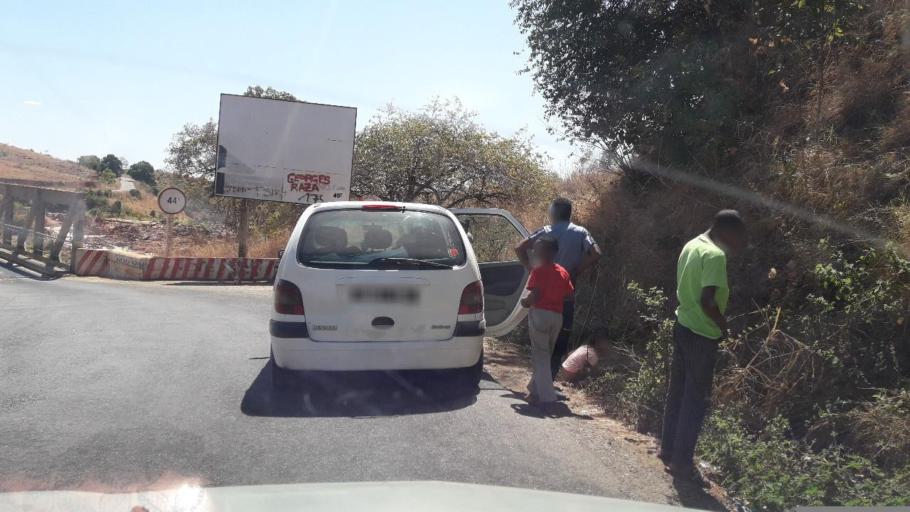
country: MG
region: Betsiboka
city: Maevatanana
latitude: -16.9380
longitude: 46.9515
